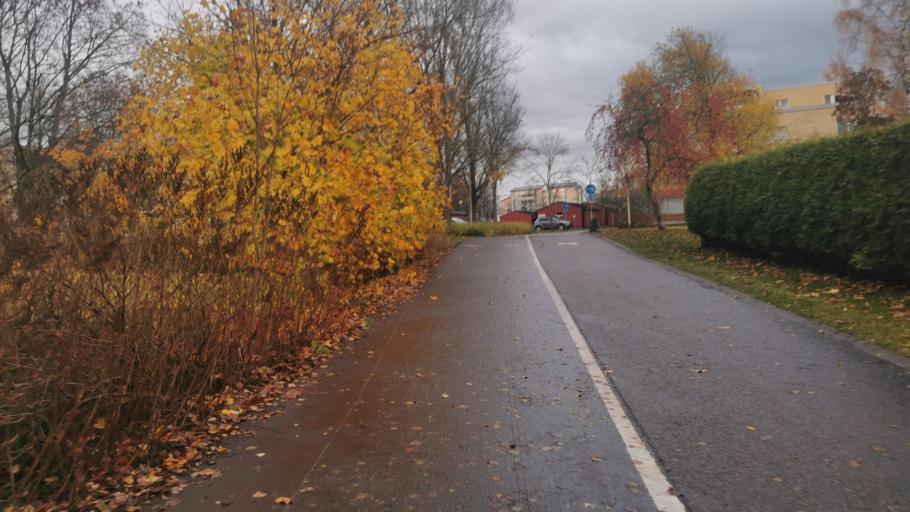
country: FI
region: Uusimaa
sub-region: Helsinki
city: Kerava
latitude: 60.4067
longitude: 25.0906
